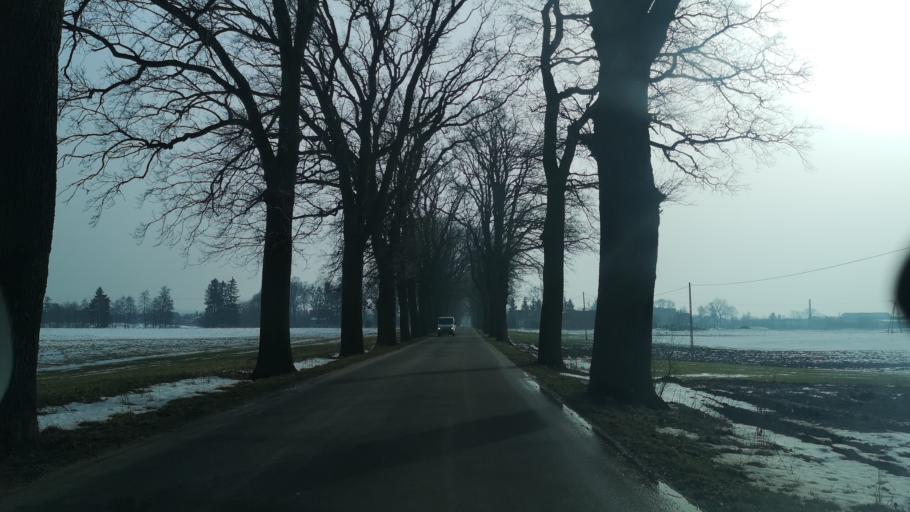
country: PL
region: Warmian-Masurian Voivodeship
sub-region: Powiat nowomiejski
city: Biskupiec
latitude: 53.5079
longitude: 19.3512
